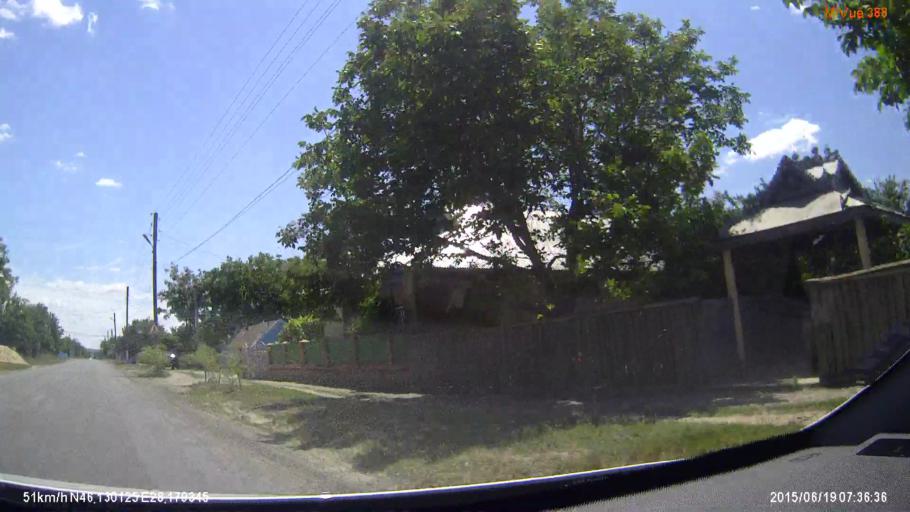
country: RO
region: Vaslui
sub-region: Oras Murgeni
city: Carja
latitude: 46.1305
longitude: 28.1792
